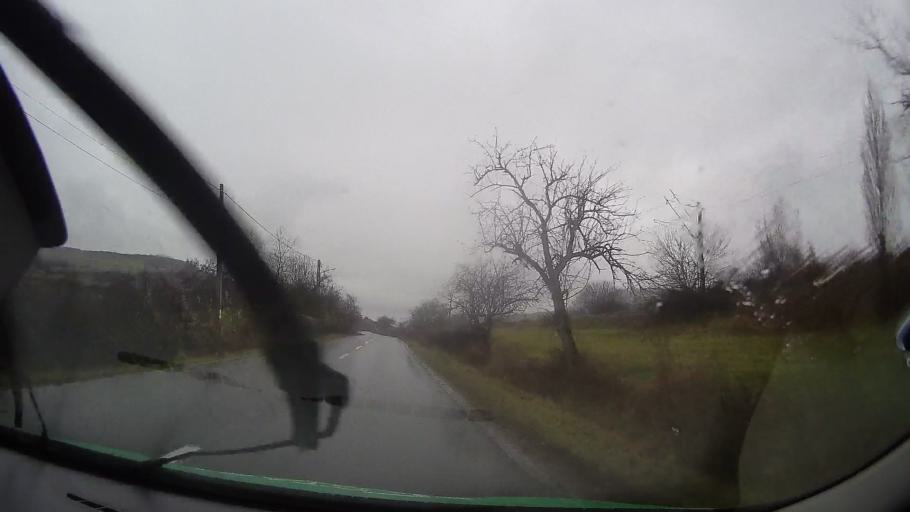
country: RO
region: Bistrita-Nasaud
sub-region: Comuna Mariselu
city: Mariselu
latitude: 47.0150
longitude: 24.5482
